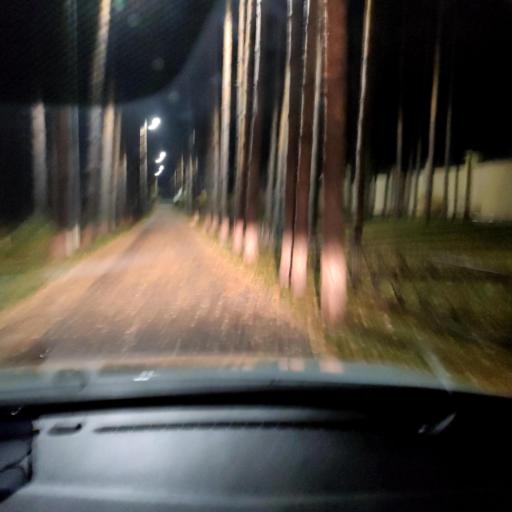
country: RU
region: Tatarstan
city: Verkhniy Uslon
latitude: 55.6219
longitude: 49.0202
